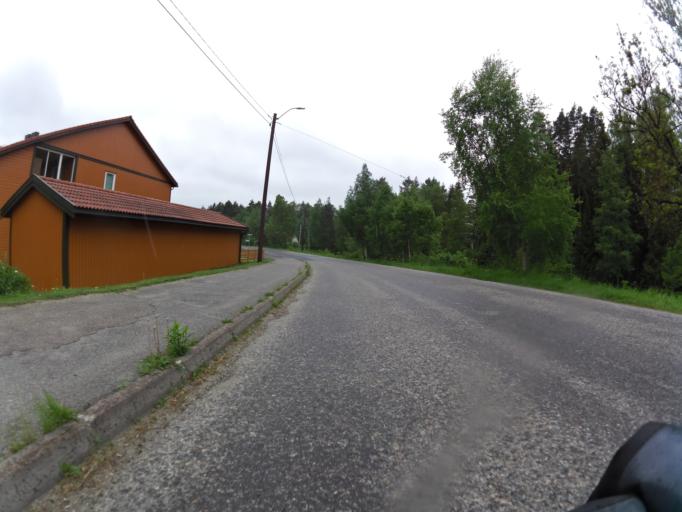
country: NO
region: Ostfold
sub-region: Rygge
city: Ryggebyen
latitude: 59.3717
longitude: 10.7734
